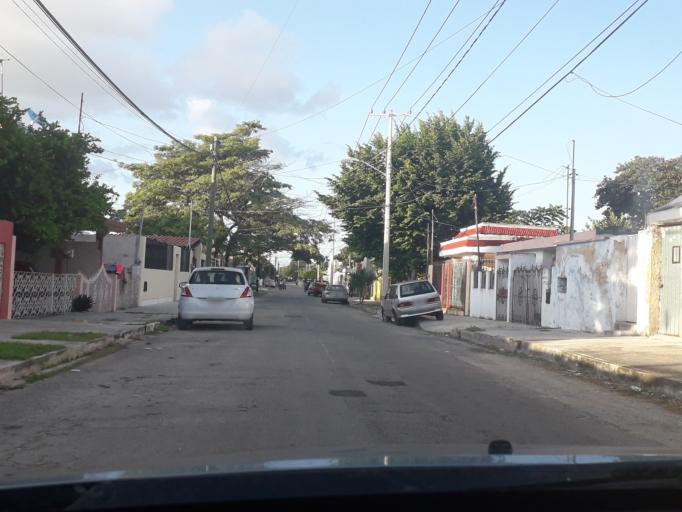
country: MX
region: Yucatan
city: Merida
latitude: 20.9725
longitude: -89.6467
